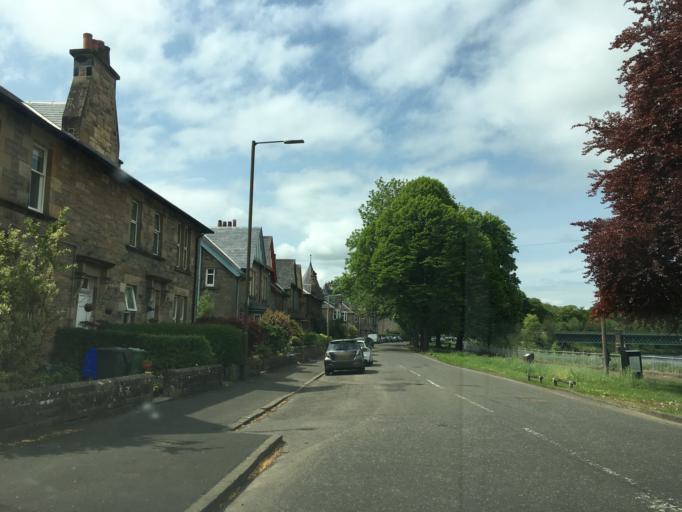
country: GB
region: Scotland
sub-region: Stirling
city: Stirling
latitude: 56.1263
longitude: -3.9295
